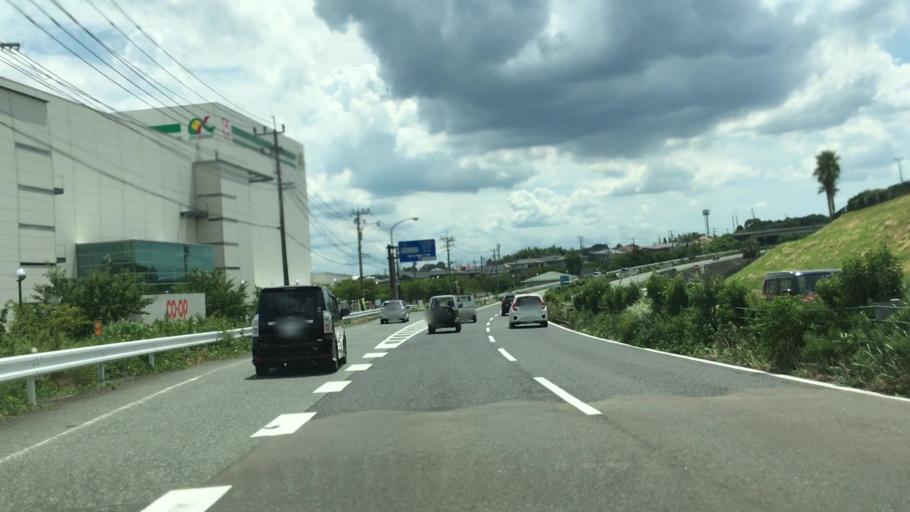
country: JP
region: Saga Prefecture
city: Tosu
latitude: 33.4052
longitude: 130.5135
